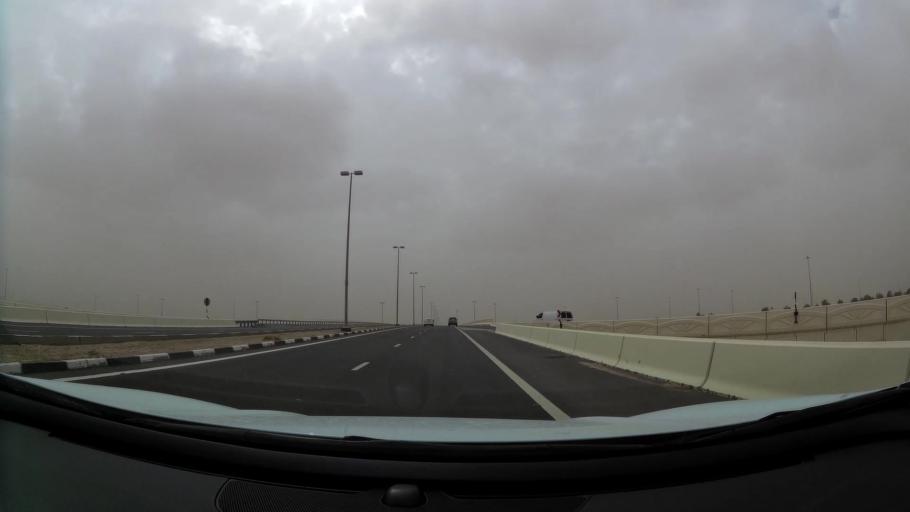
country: AE
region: Abu Dhabi
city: Abu Dhabi
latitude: 24.4162
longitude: 54.7142
